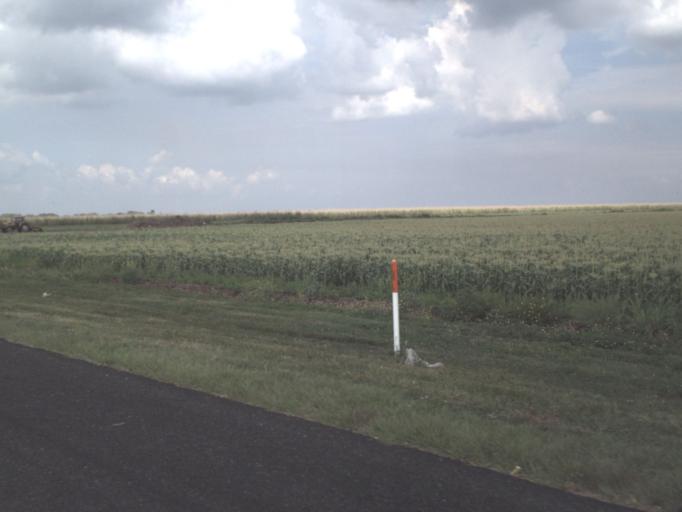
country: US
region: Florida
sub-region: Palm Beach County
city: Belle Glade
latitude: 26.7264
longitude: -80.6498
